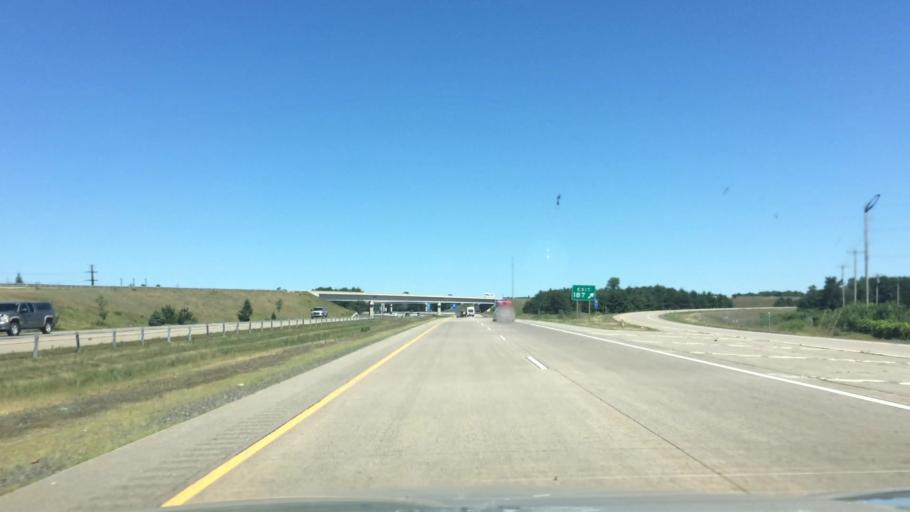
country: US
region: Wisconsin
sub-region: Marathon County
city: Rothschild
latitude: 44.8904
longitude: -89.6399
